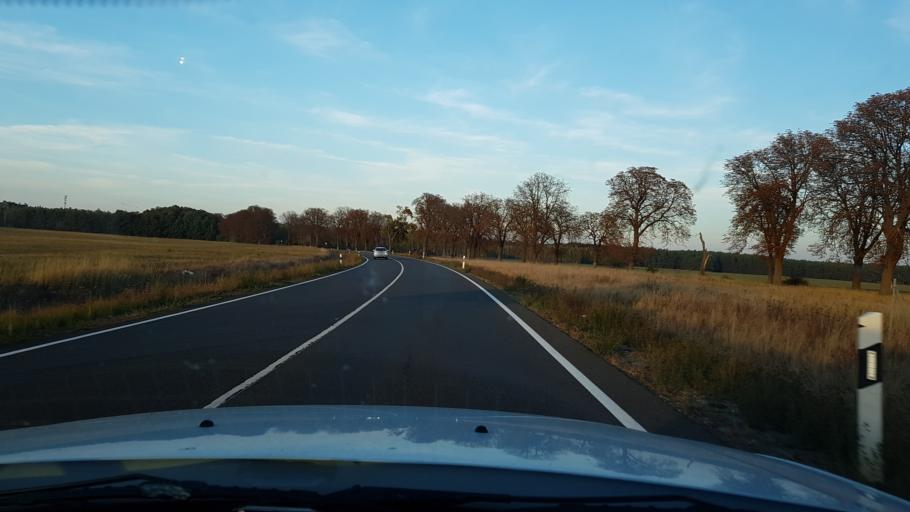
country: DE
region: Brandenburg
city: Schwedt (Oder)
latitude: 53.1069
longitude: 14.3014
